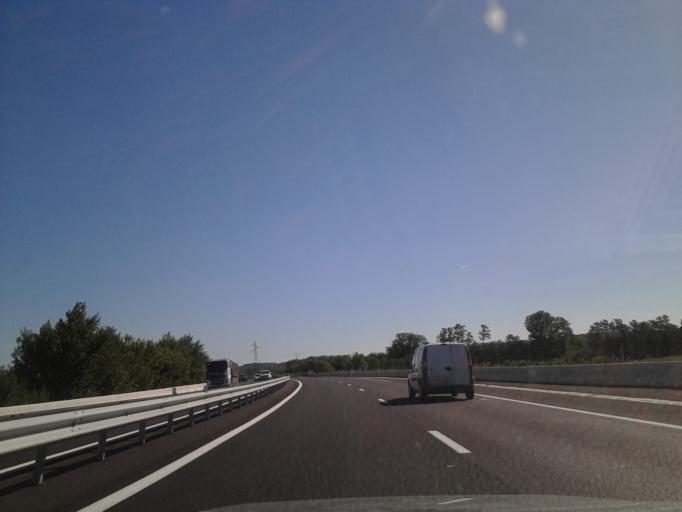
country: FR
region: Languedoc-Roussillon
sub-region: Departement de l'Herault
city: Pezenas
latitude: 43.4459
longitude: 3.4241
